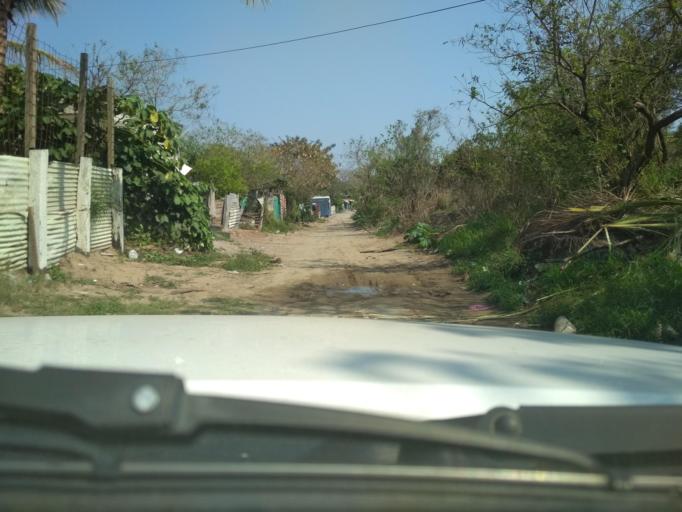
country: MX
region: Veracruz
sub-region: Veracruz
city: Colonia Chalchihuecan
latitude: 19.2124
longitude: -96.2122
